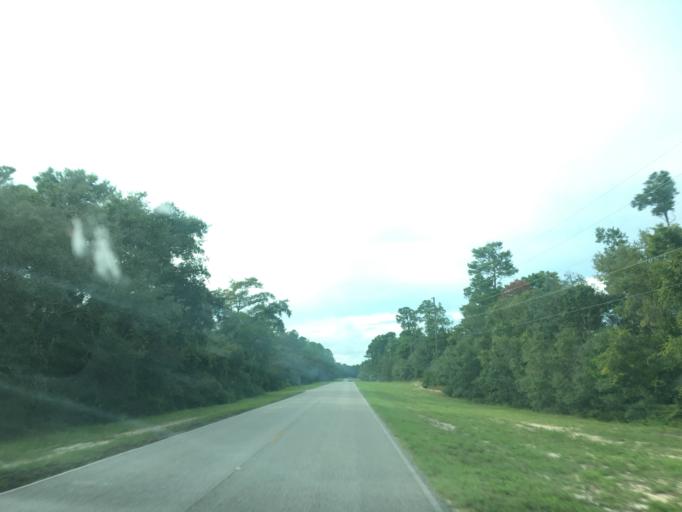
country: US
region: Florida
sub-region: Wakulla County
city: Crawfordville
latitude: 29.9221
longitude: -84.3732
